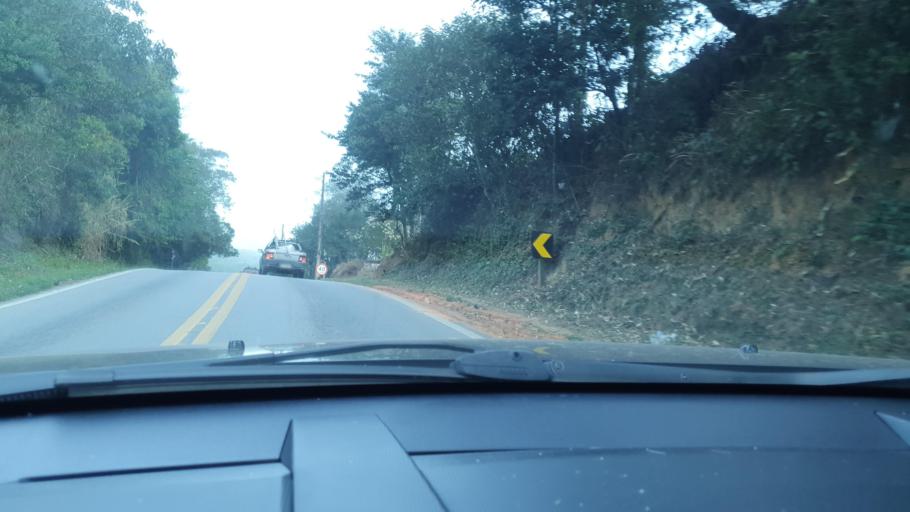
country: BR
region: Sao Paulo
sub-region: Ibiuna
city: Ibiuna
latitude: -23.6837
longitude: -47.2692
